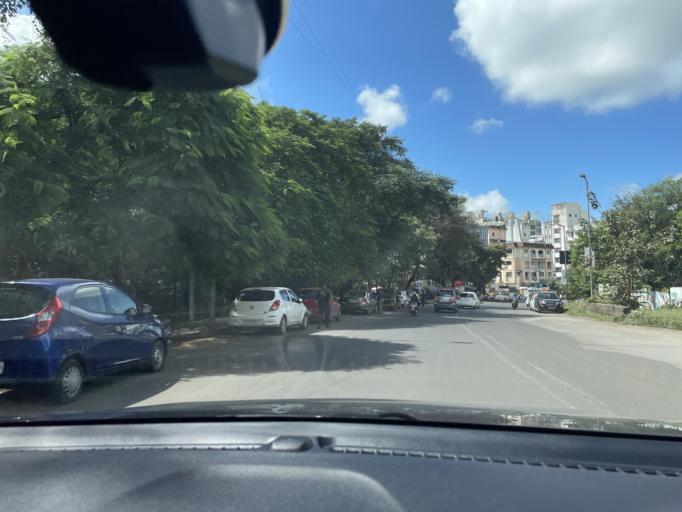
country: IN
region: Maharashtra
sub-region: Pune Division
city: Shivaji Nagar
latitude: 18.5185
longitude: 73.7793
